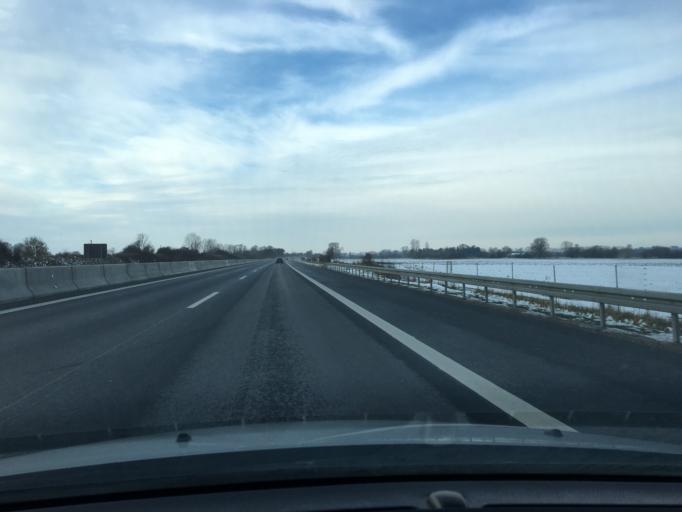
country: DE
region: Bavaria
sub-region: Upper Bavaria
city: Langenpreising
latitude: 48.4227
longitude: 11.9301
